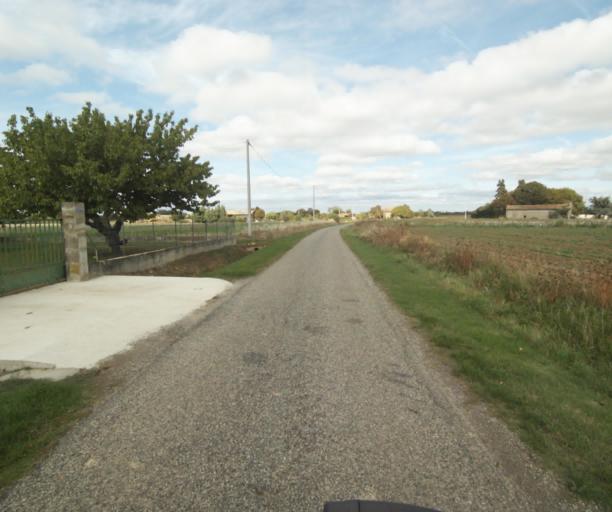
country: FR
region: Midi-Pyrenees
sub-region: Departement du Tarn-et-Garonne
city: Saint-Porquier
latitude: 43.9515
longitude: 1.1516
